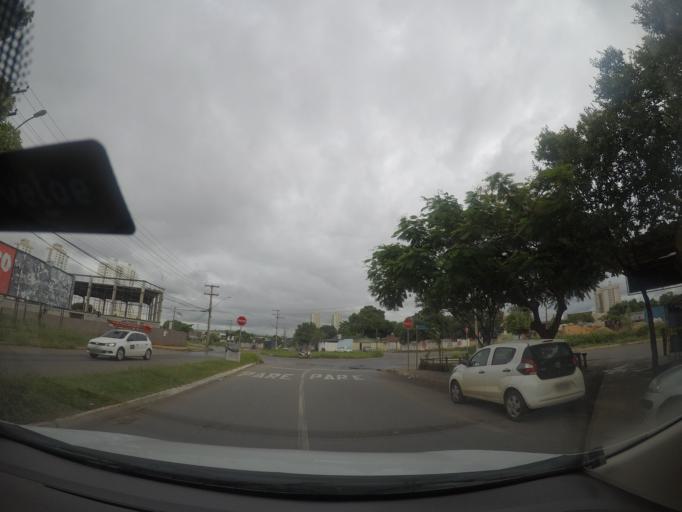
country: BR
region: Goias
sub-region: Goiania
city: Goiania
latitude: -16.7338
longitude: -49.2878
